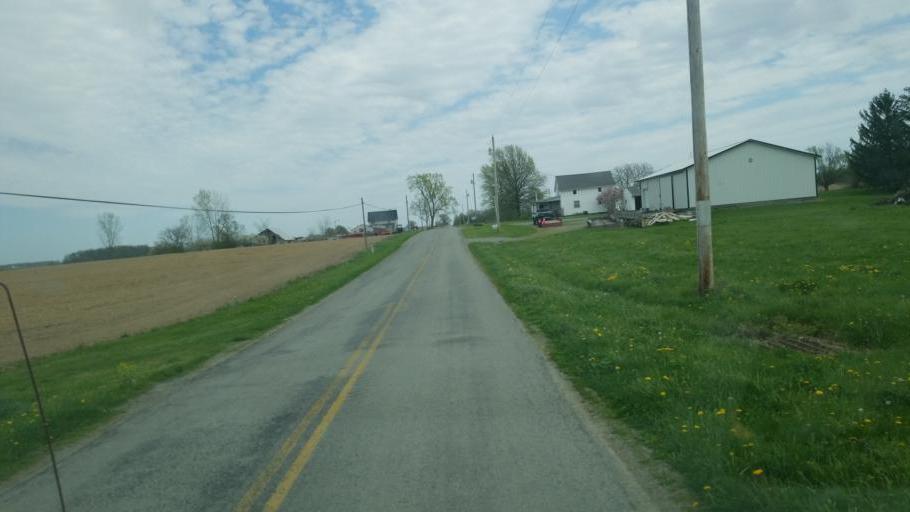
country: US
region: Ohio
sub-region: Hardin County
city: Ada
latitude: 40.8198
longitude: -83.8365
